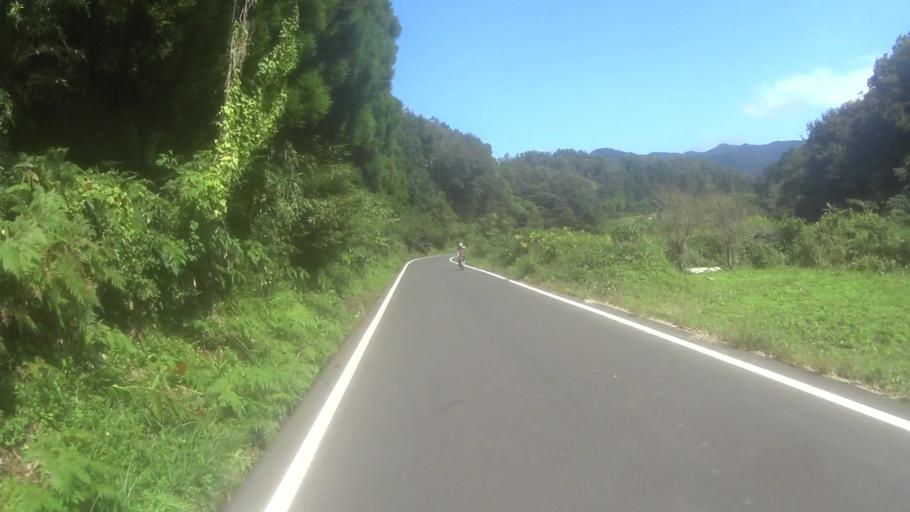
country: JP
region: Kyoto
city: Miyazu
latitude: 35.6116
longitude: 135.1177
